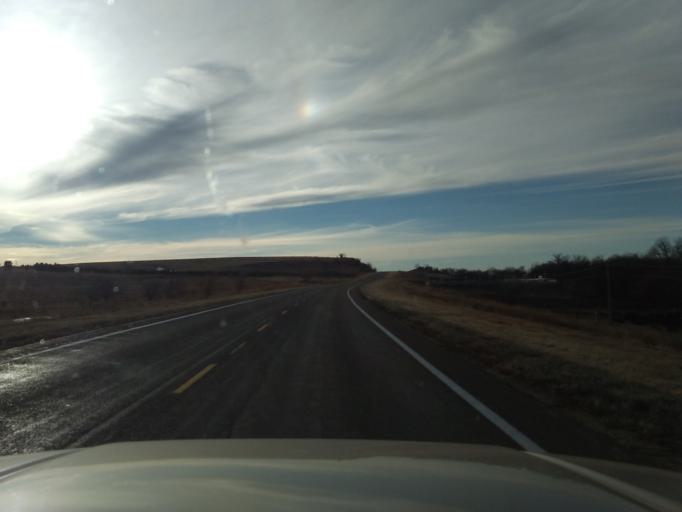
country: US
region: Kansas
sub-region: Norton County
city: Norton
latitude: 39.7216
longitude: -100.1941
